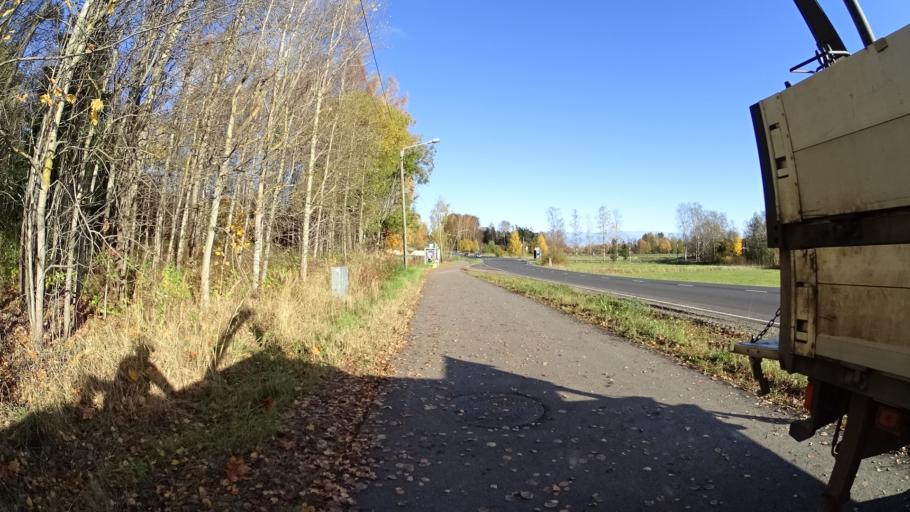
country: FI
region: Uusimaa
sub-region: Helsinki
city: Teekkarikylae
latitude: 60.2991
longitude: 24.8582
